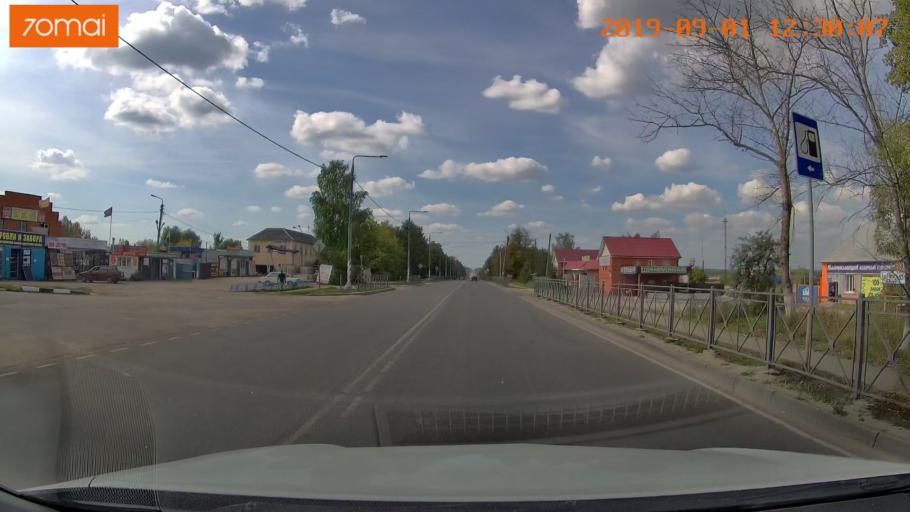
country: RU
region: Kaluga
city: Maloyaroslavets
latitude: 55.0050
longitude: 36.4362
